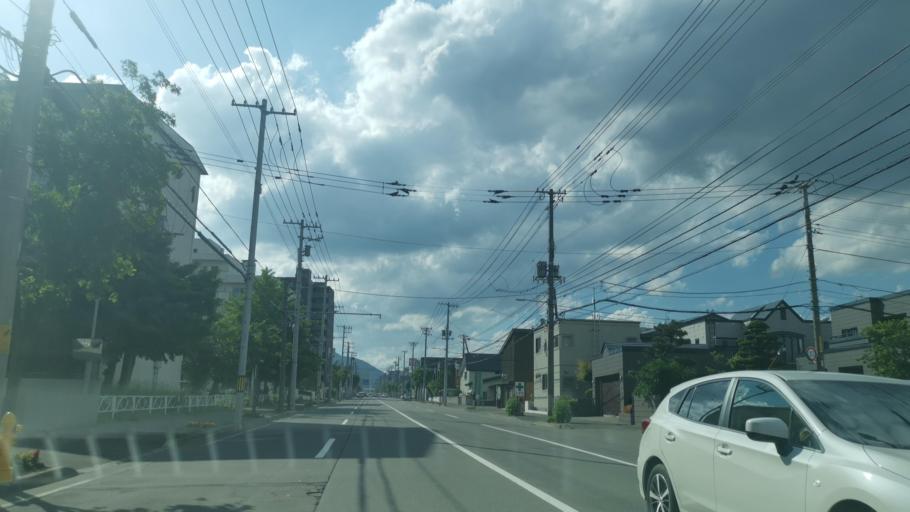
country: JP
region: Hokkaido
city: Sapporo
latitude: 43.0661
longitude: 141.2980
